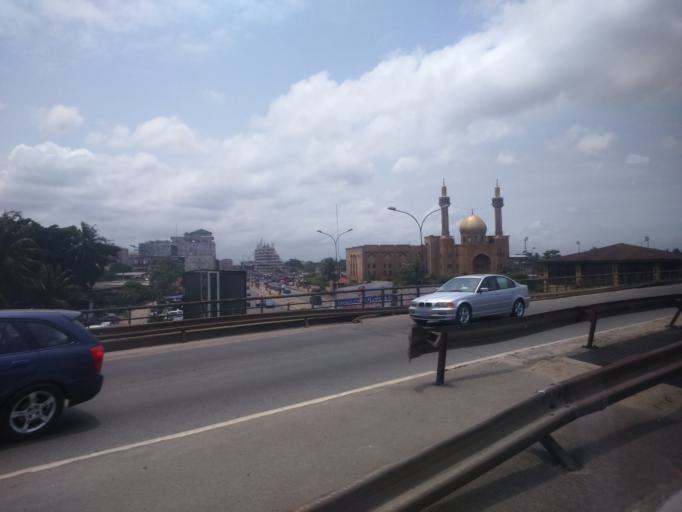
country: CI
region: Lagunes
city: Abidjan
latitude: 5.3064
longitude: -3.9971
